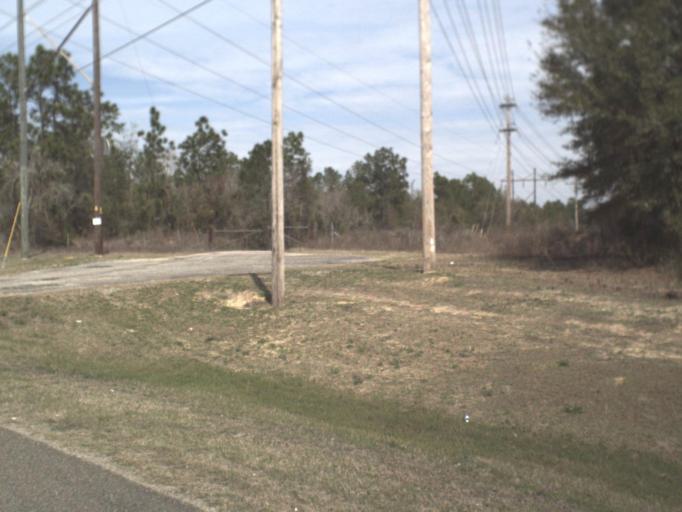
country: US
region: Florida
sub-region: Leon County
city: Tallahassee
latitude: 30.3887
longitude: -84.3149
